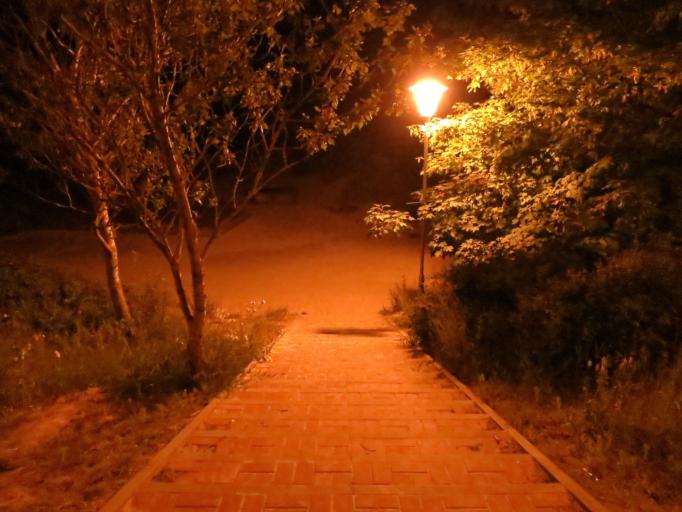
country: LV
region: Liepaja
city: Liepaja
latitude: 56.5005
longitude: 20.9944
